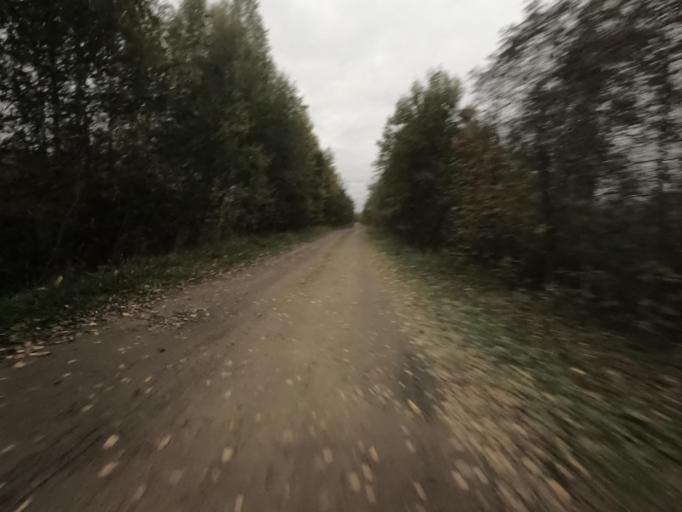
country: RU
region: Leningrad
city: Kirovsk
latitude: 59.8351
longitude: 30.9818
